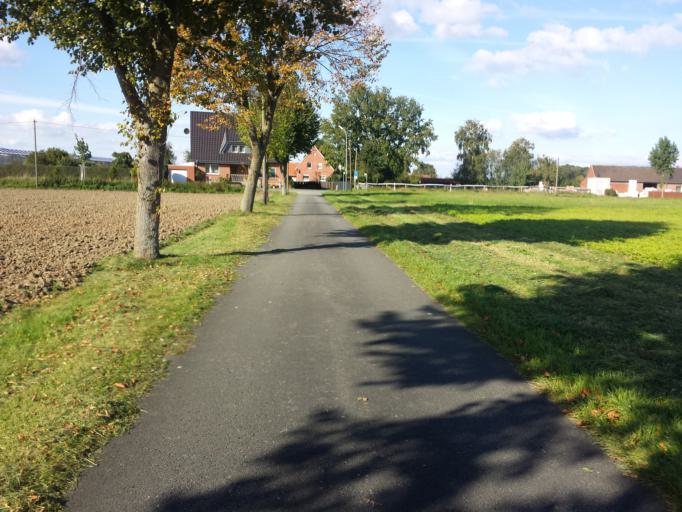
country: DE
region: North Rhine-Westphalia
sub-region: Regierungsbezirk Detmold
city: Langenberg
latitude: 51.7499
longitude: 8.3159
